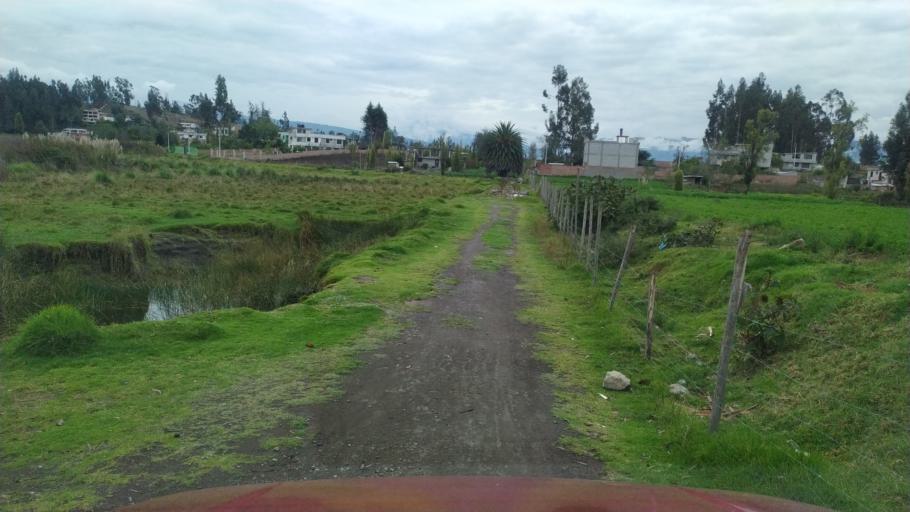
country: EC
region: Chimborazo
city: Riobamba
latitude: -1.6539
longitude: -78.6396
